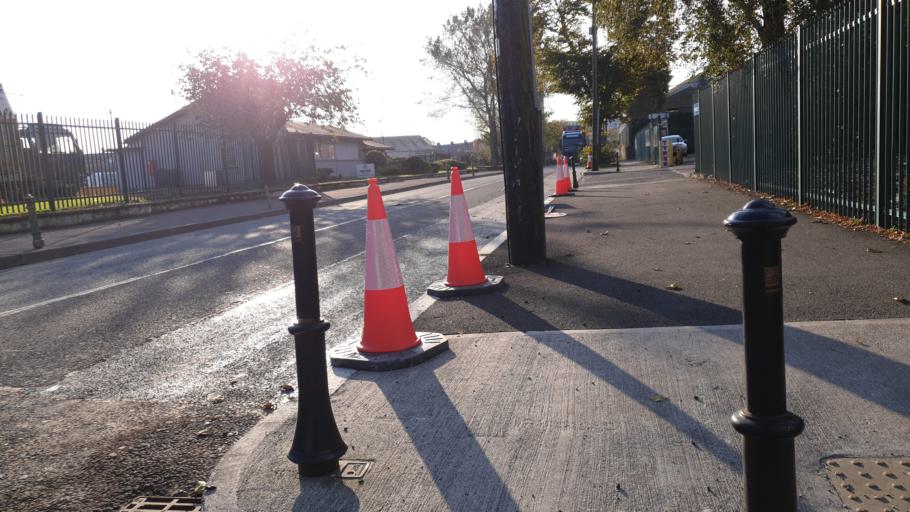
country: IE
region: Munster
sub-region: County Cork
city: Cork
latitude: 51.8974
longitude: -8.4552
